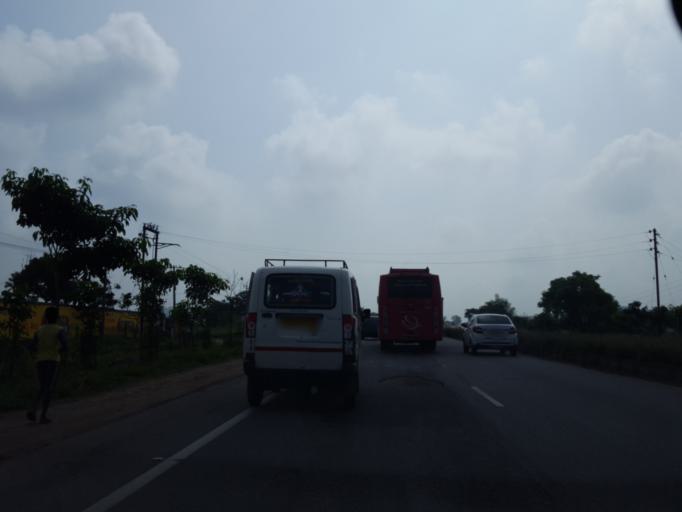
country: IN
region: Telangana
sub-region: Rangareddi
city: Ghatkesar
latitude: 17.2911
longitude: 78.7634
